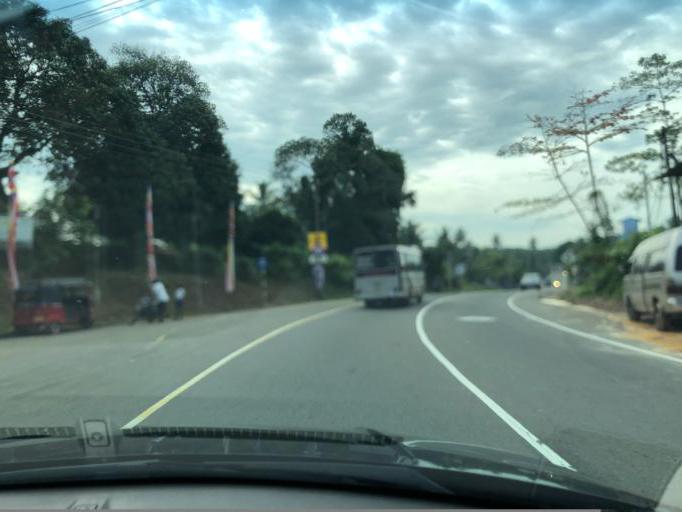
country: LK
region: Western
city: Kalutara
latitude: 6.5596
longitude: 80.0116
